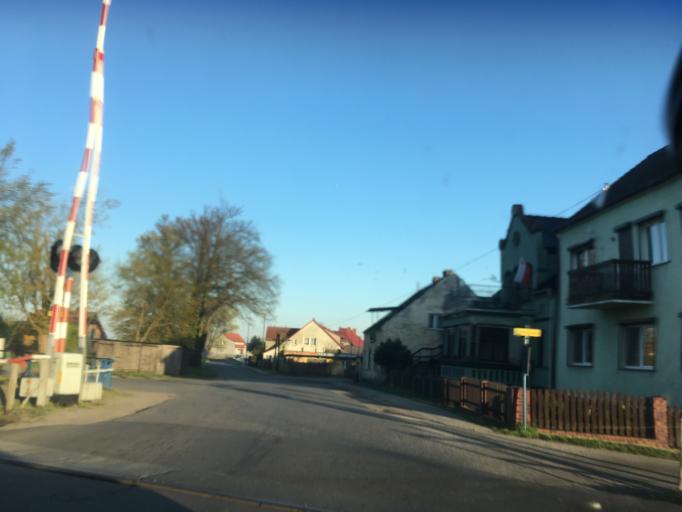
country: PL
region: Lubusz
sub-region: Powiat gorzowski
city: Bogdaniec
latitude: 52.6875
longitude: 15.0731
